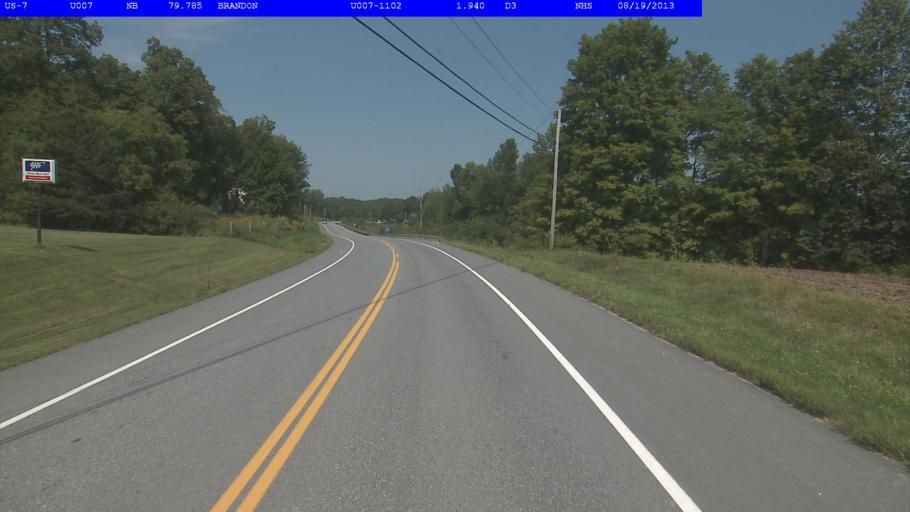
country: US
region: Vermont
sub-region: Rutland County
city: Brandon
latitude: 43.7808
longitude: -73.0588
